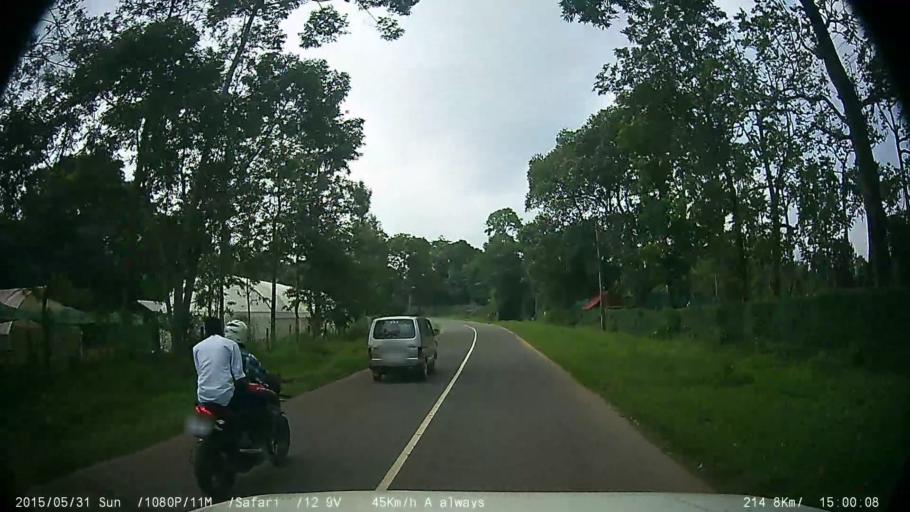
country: IN
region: Kerala
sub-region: Wayanad
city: Kalpetta
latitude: 11.6145
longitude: 76.2115
